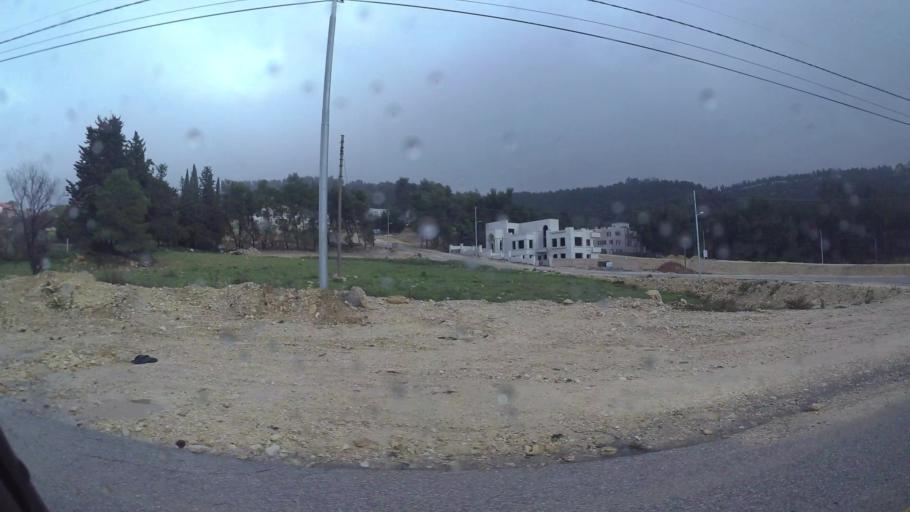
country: JO
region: Amman
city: Al Jubayhah
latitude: 32.0157
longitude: 35.8089
